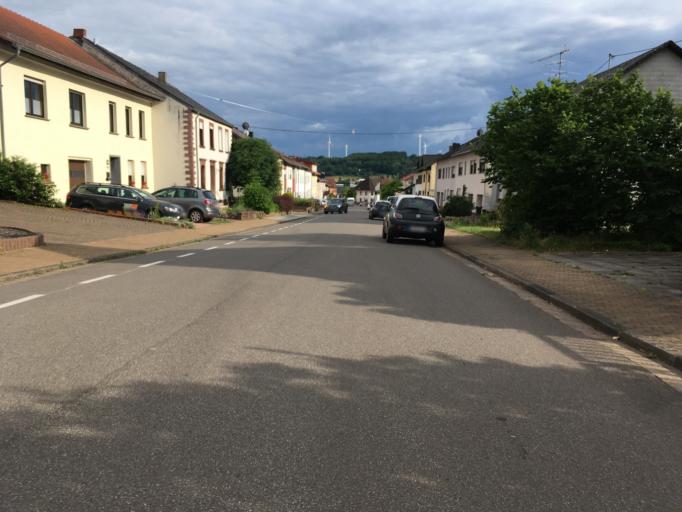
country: DE
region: Saarland
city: Losheim
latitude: 49.5138
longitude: 6.7464
